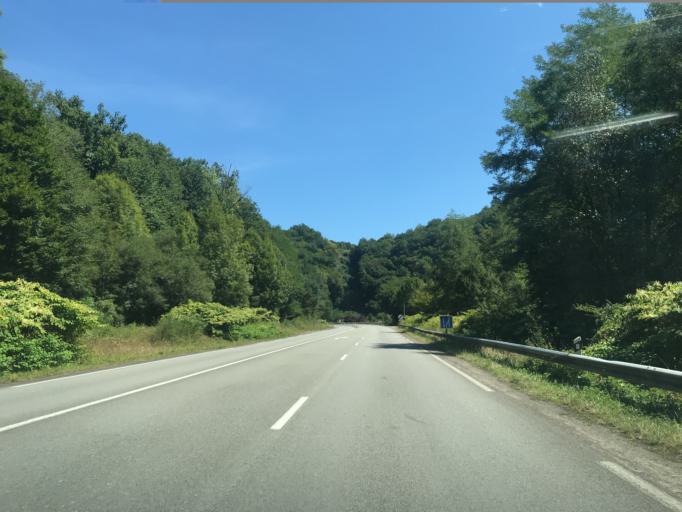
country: FR
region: Limousin
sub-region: Departement de la Correze
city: Chameyrat
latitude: 45.2251
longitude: 1.7068
